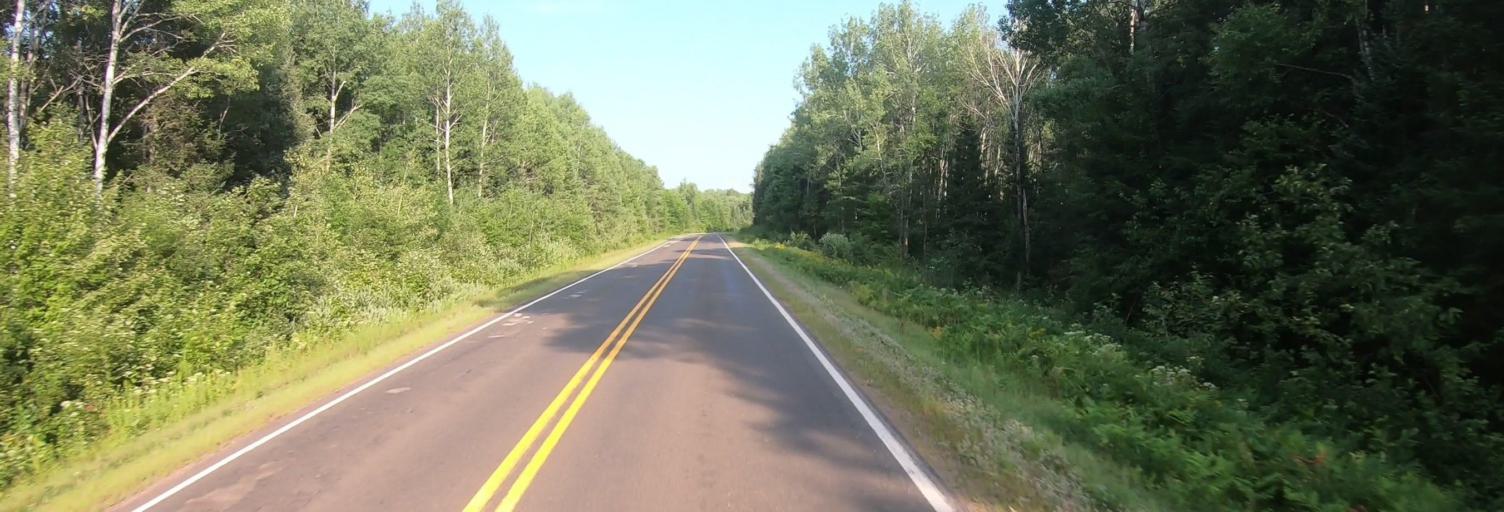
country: US
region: Wisconsin
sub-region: Ashland County
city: Ashland
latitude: 46.2559
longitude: -90.8362
